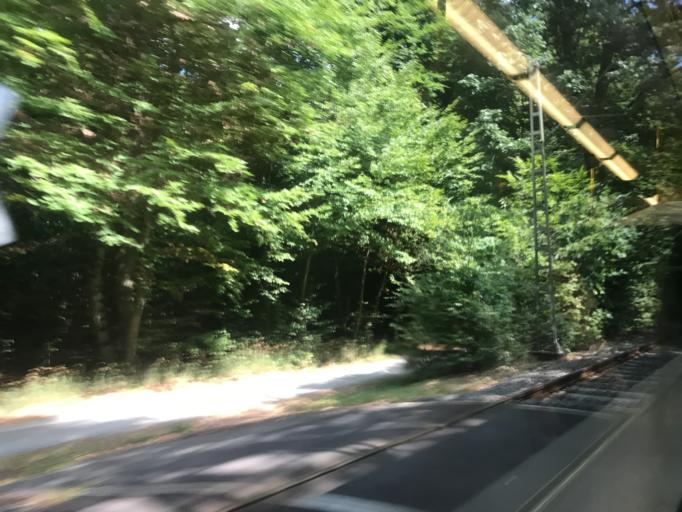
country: DE
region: Hesse
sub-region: Regierungsbezirk Darmstadt
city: Neu Isenburg
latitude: 50.0671
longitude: 8.6857
